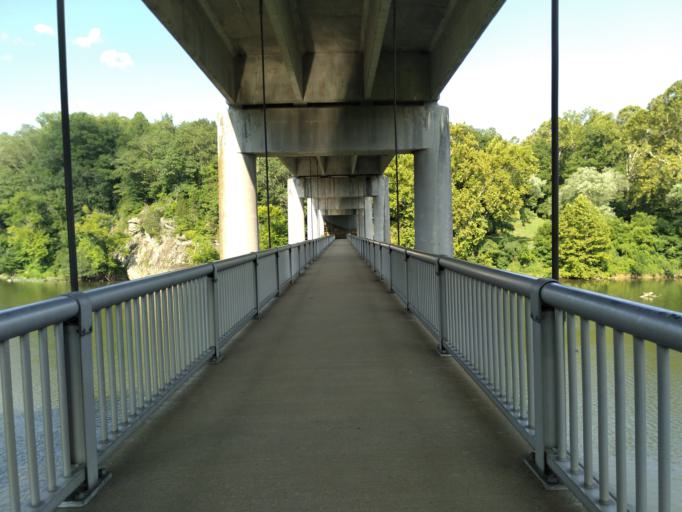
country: US
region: Virginia
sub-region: Rockbridge County
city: Glasgow
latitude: 37.5552
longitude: -79.3678
